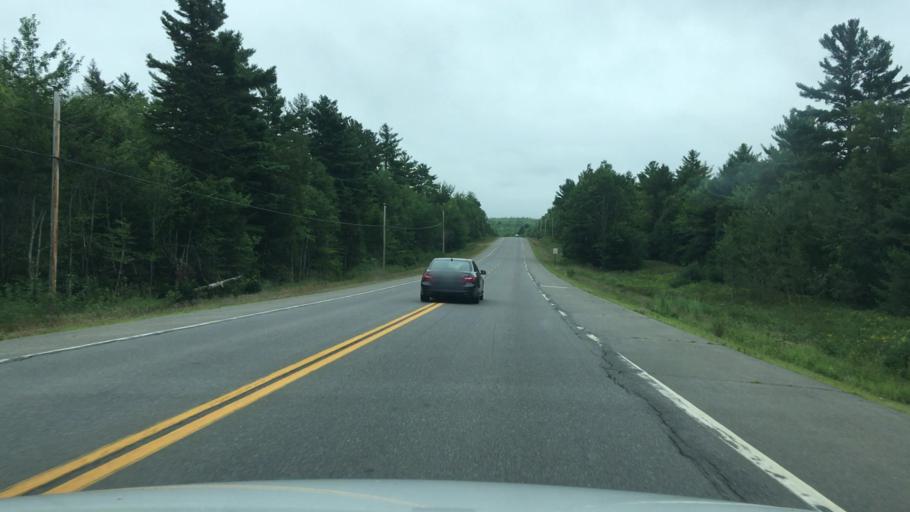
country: US
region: Maine
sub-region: Hancock County
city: Franklin
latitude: 44.8366
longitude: -68.1428
